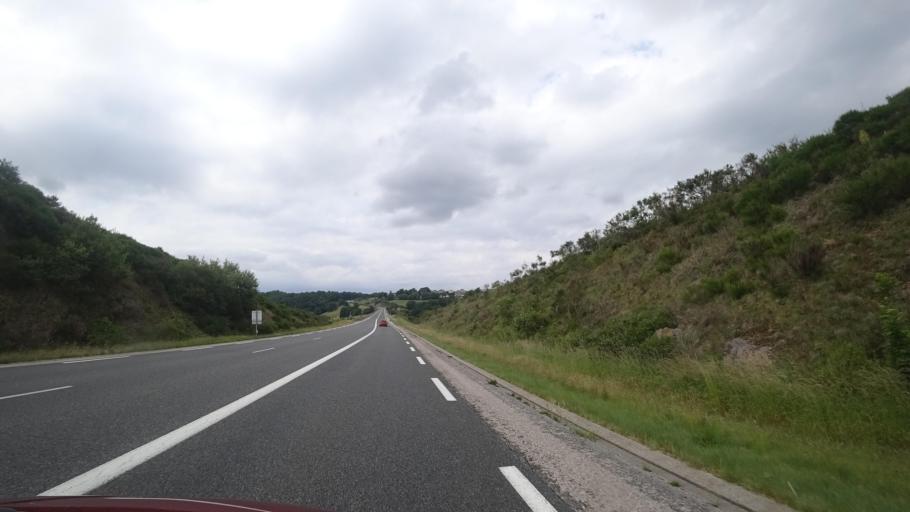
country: FR
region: Midi-Pyrenees
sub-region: Departement de l'Aveyron
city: Pont-de-Salars
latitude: 44.2793
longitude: 2.7218
